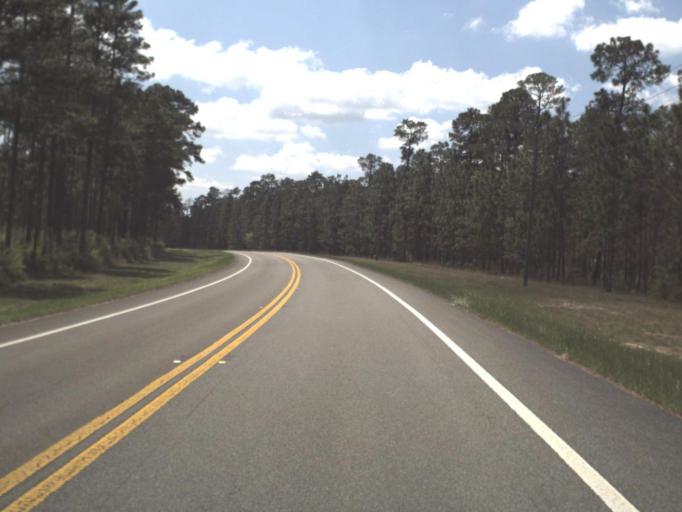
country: US
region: Florida
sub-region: Okaloosa County
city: Crestview
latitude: 30.9096
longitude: -86.6536
